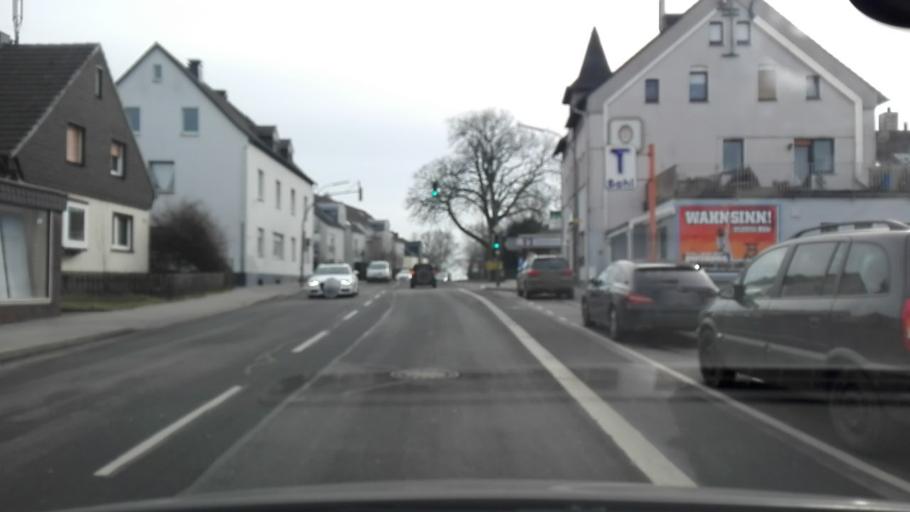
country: DE
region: North Rhine-Westphalia
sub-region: Regierungsbezirk Arnsberg
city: Holzwickede
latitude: 51.4783
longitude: 7.5977
